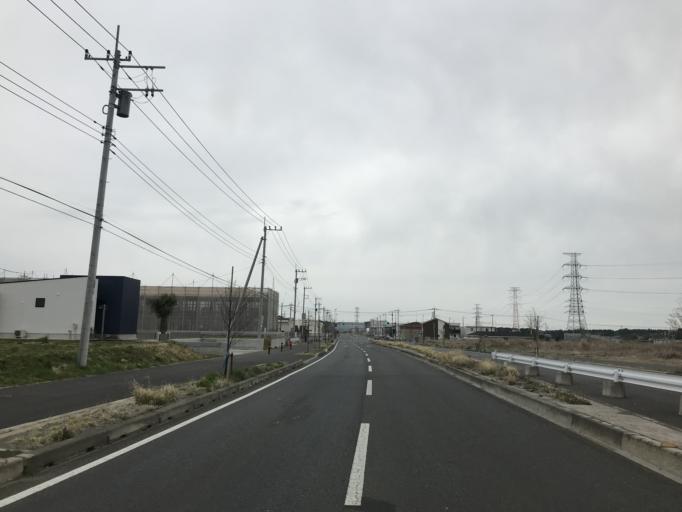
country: JP
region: Ibaraki
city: Mitsukaido
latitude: 36.0165
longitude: 140.0645
